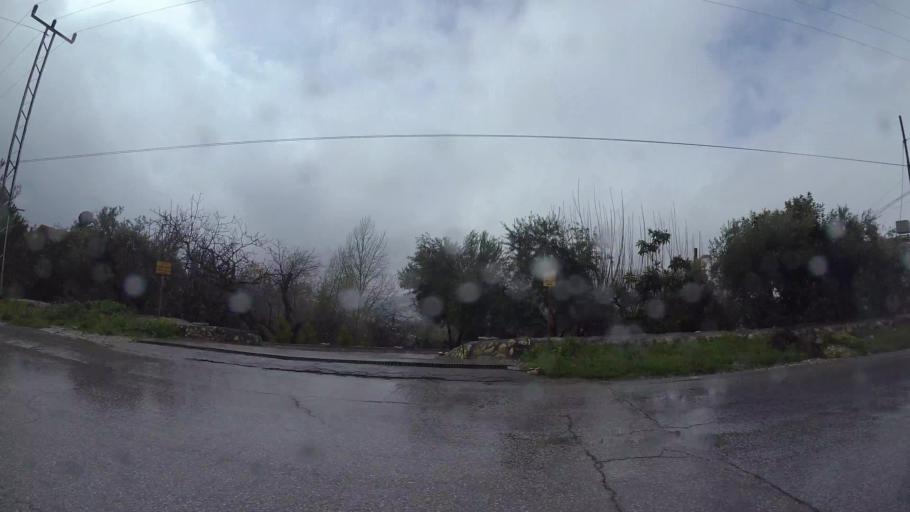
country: JO
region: Amman
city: Wadi as Sir
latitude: 32.0110
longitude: 35.7968
